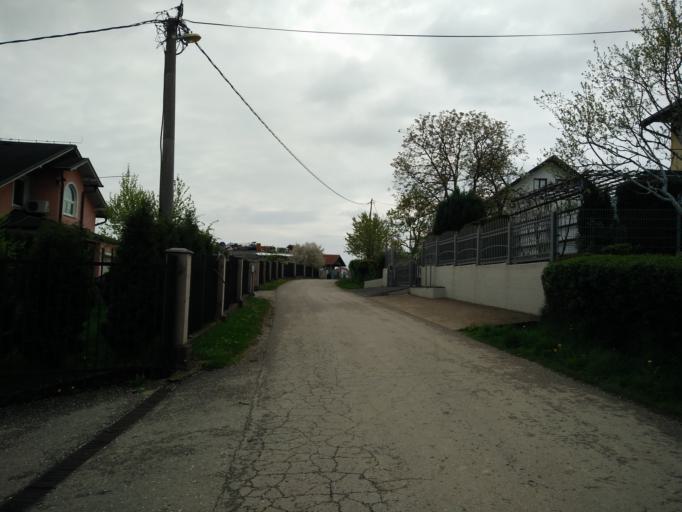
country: BA
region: Republika Srpska
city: Prijedor
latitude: 44.9981
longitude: 16.7489
